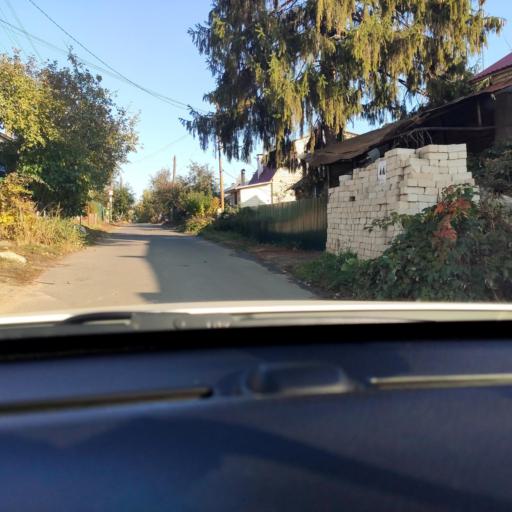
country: RU
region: Voronezj
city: Voronezh
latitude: 51.7079
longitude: 39.2387
